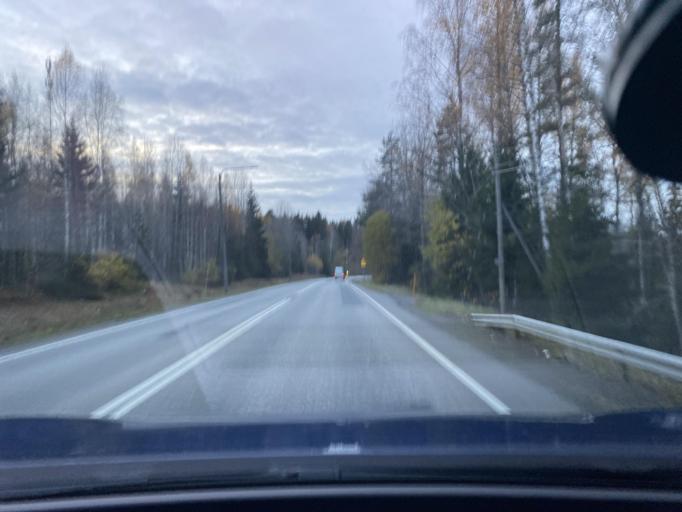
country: FI
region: Uusimaa
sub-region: Helsinki
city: Vihti
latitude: 60.3344
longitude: 24.2040
